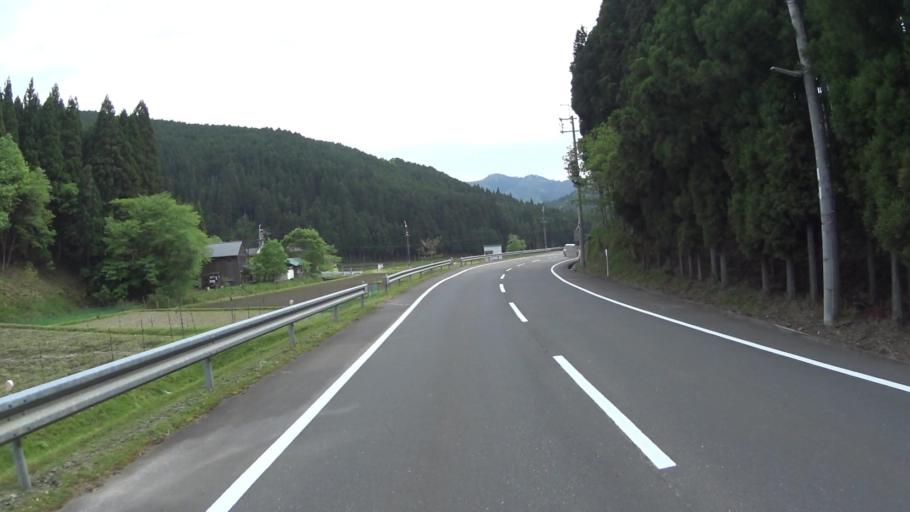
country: JP
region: Kyoto
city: Kameoka
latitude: 35.1443
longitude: 135.6159
